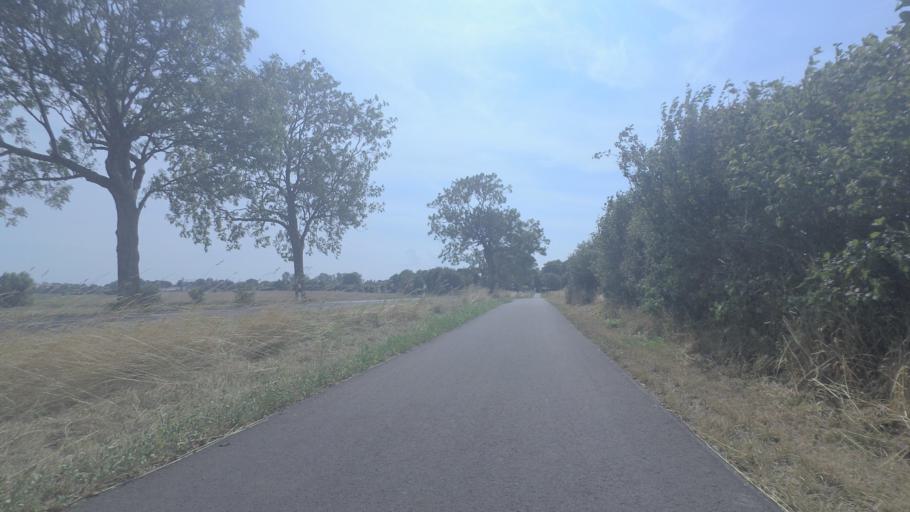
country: DE
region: Mecklenburg-Vorpommern
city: Garz
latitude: 54.2550
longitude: 13.3497
